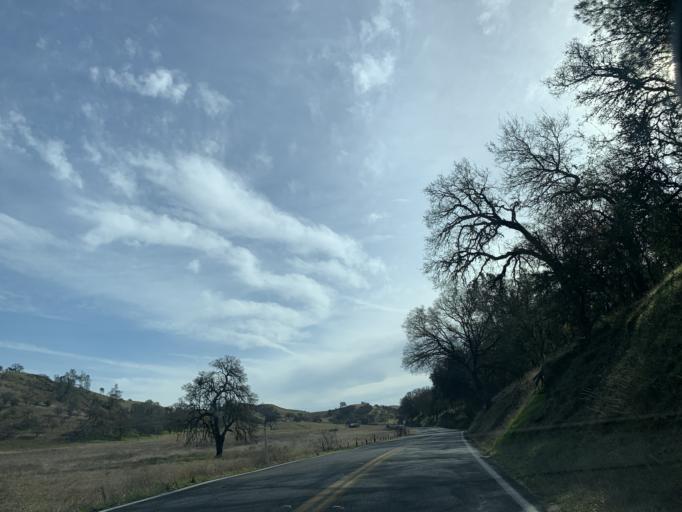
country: US
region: California
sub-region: Monterey County
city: Soledad
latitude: 36.5113
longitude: -121.1161
